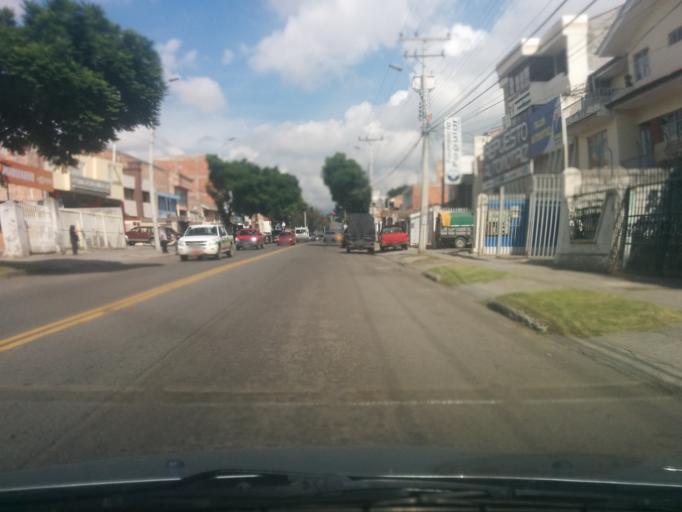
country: EC
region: Azuay
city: Cuenca
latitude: -2.8994
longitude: -78.9894
